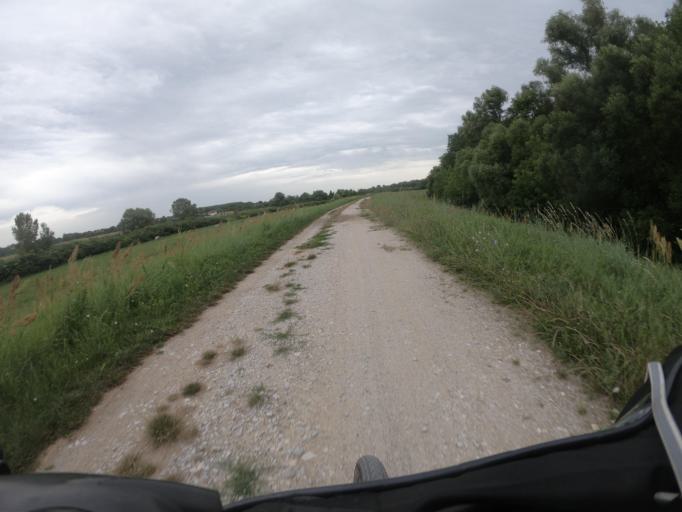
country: HU
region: Jasz-Nagykun-Szolnok
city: Tiszafured
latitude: 47.6848
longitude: 20.8029
